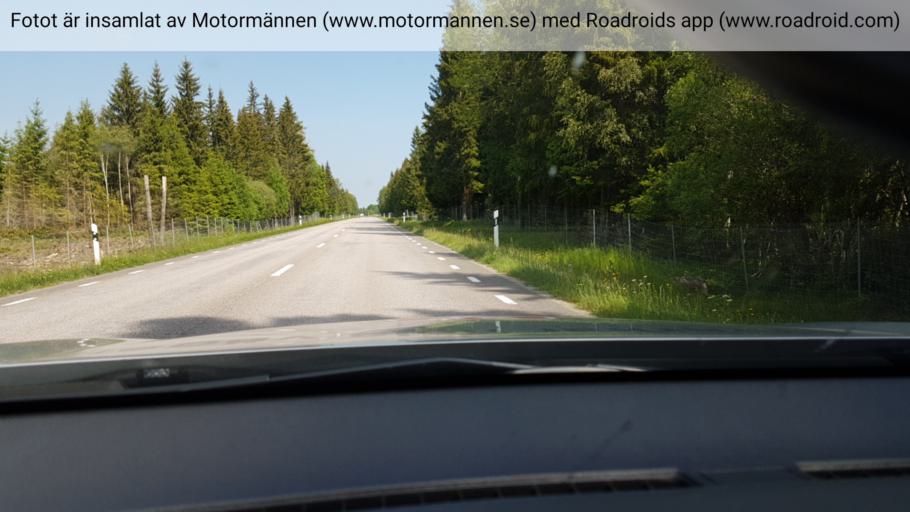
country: SE
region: Vaestra Goetaland
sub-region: Falkopings Kommun
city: Falkoeping
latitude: 58.0375
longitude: 13.5474
